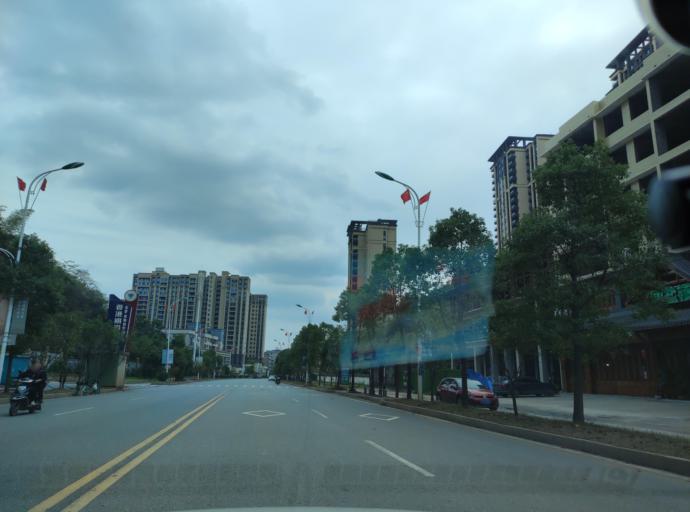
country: CN
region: Jiangxi Sheng
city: Pingxiang
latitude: 27.6786
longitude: 113.9081
